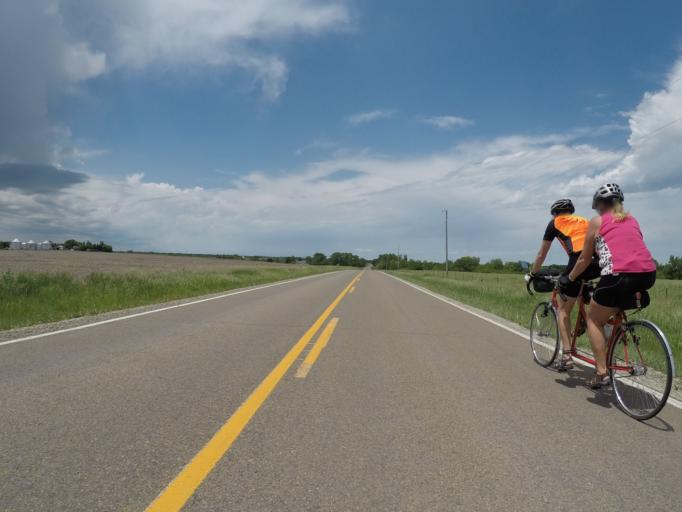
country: US
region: Kansas
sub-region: Morris County
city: Council Grove
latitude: 38.8544
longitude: -96.4408
